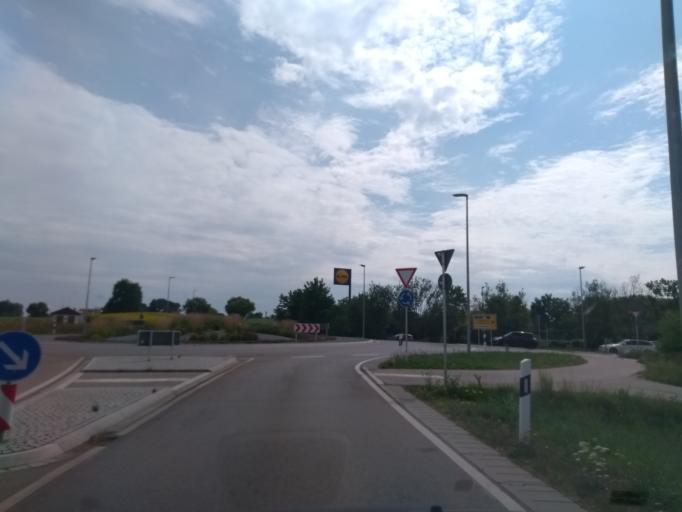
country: DE
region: Bavaria
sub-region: Upper Bavaria
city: Markt Indersdorf
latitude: 48.3472
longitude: 11.3845
